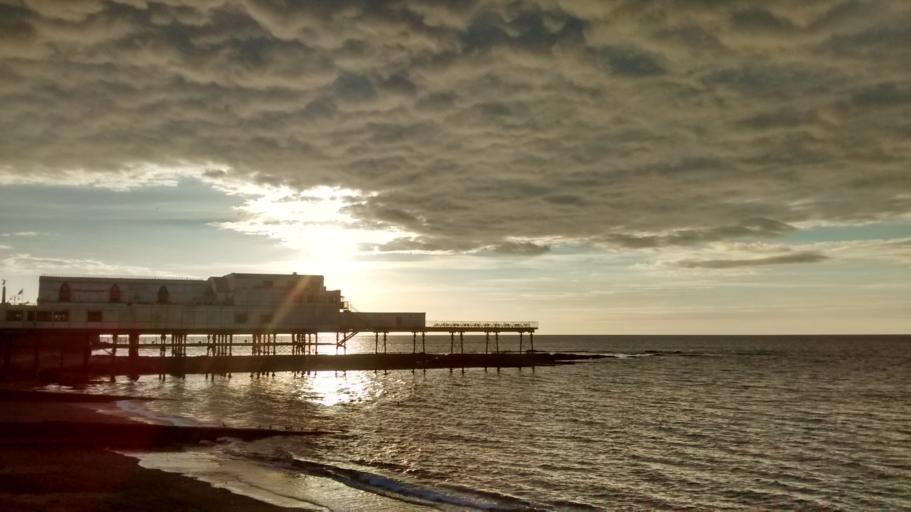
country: GB
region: Wales
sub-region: County of Ceredigion
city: Aberystwyth
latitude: 52.4165
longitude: -4.0856
